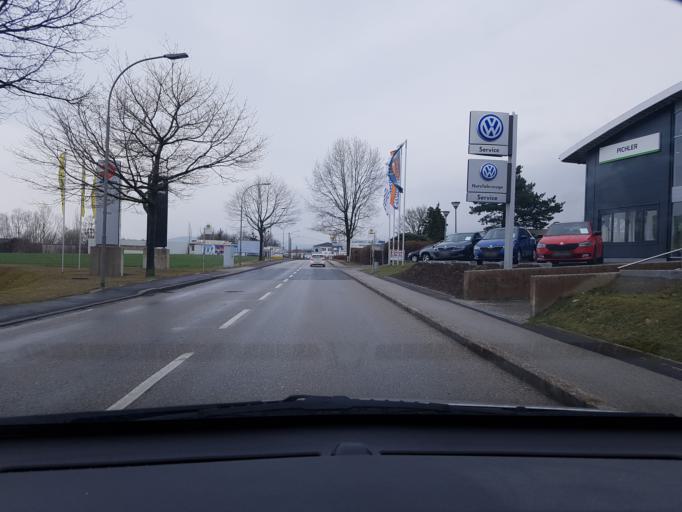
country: AT
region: Upper Austria
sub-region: Steyr Stadt
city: Steyr
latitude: 48.0492
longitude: 14.4028
